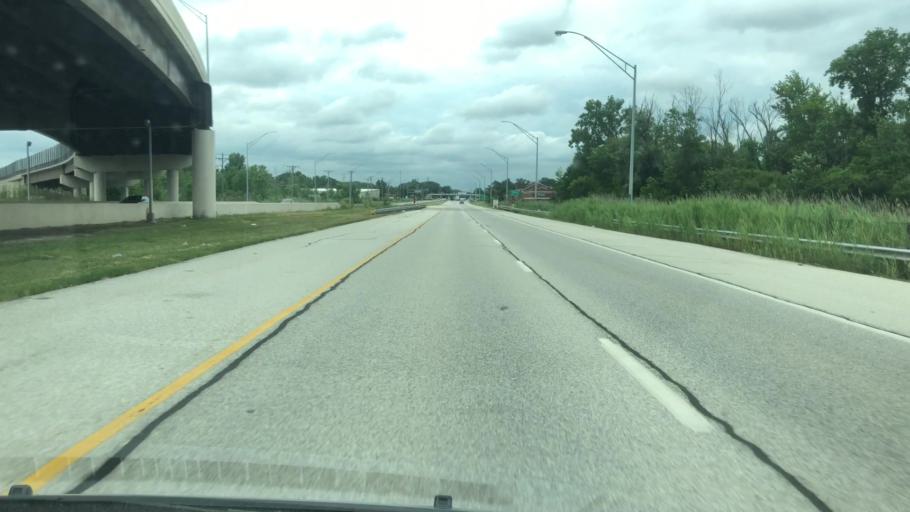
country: US
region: Ohio
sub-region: Summit County
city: Macedonia
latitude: 41.2930
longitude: -81.5114
